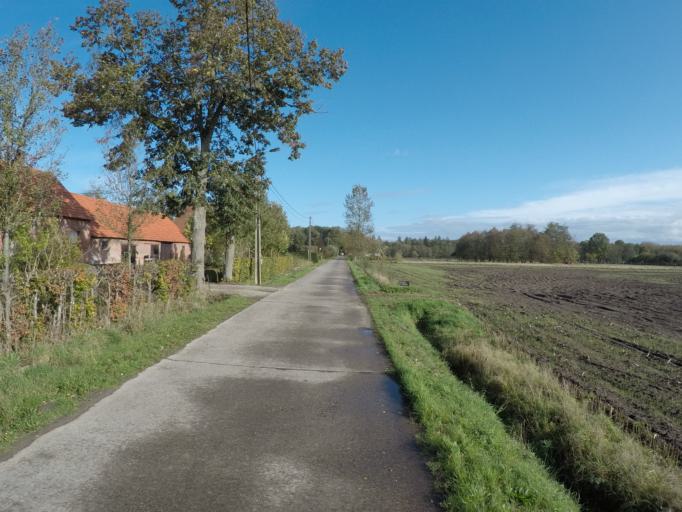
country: BE
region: Flanders
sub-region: Provincie Antwerpen
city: Zandhoven
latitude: 51.2492
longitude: 4.6637
